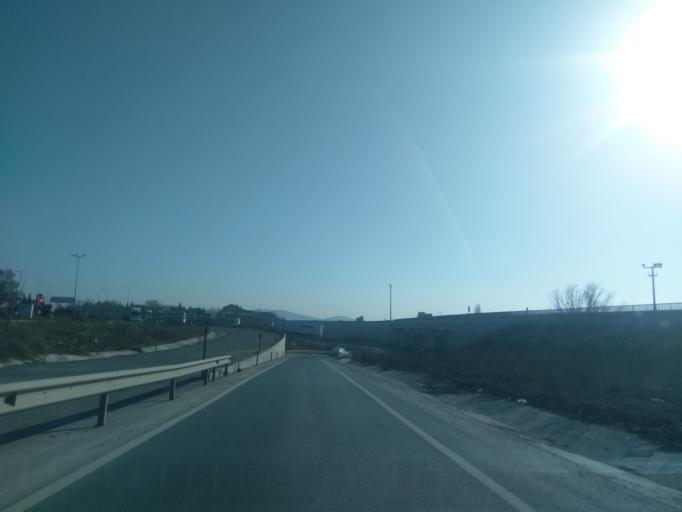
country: TR
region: Istanbul
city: Muratbey
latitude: 41.0881
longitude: 28.5144
